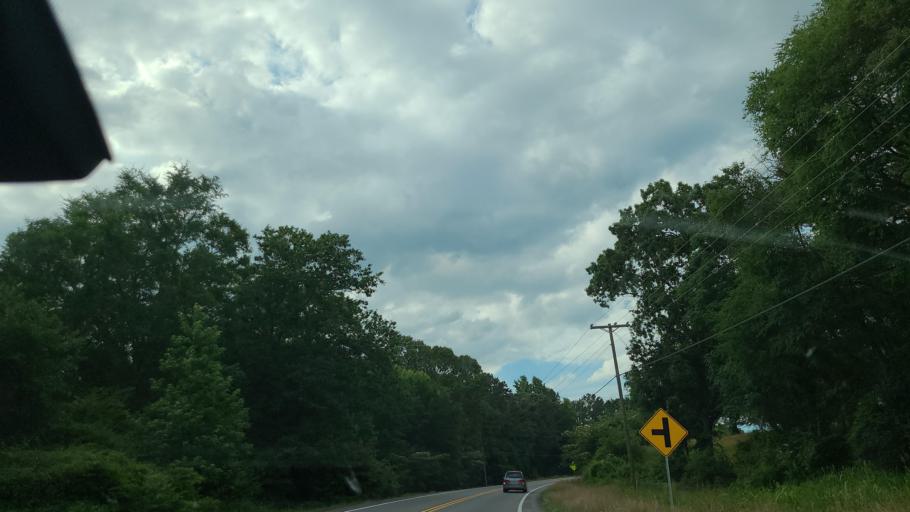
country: US
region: Georgia
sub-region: Putnam County
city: Eatonton
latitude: 33.2333
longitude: -83.4352
